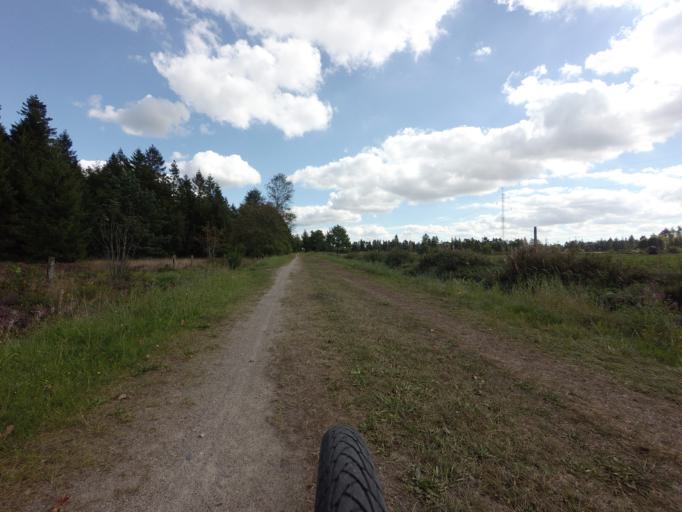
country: DK
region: Central Jutland
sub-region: Ikast-Brande Kommune
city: Brande
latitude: 55.9764
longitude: 9.2232
